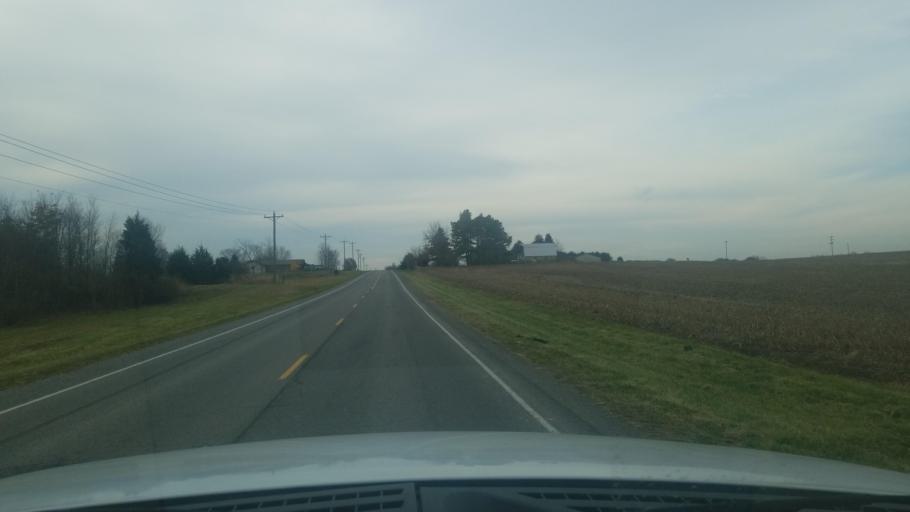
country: US
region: Illinois
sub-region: Saline County
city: Harrisburg
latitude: 37.8223
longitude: -88.6518
